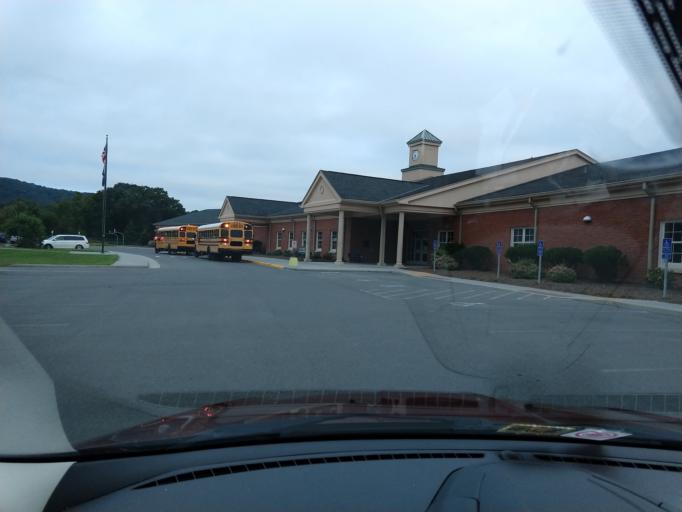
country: US
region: Virginia
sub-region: City of Covington
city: Fairlawn
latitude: 37.7523
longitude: -79.9942
